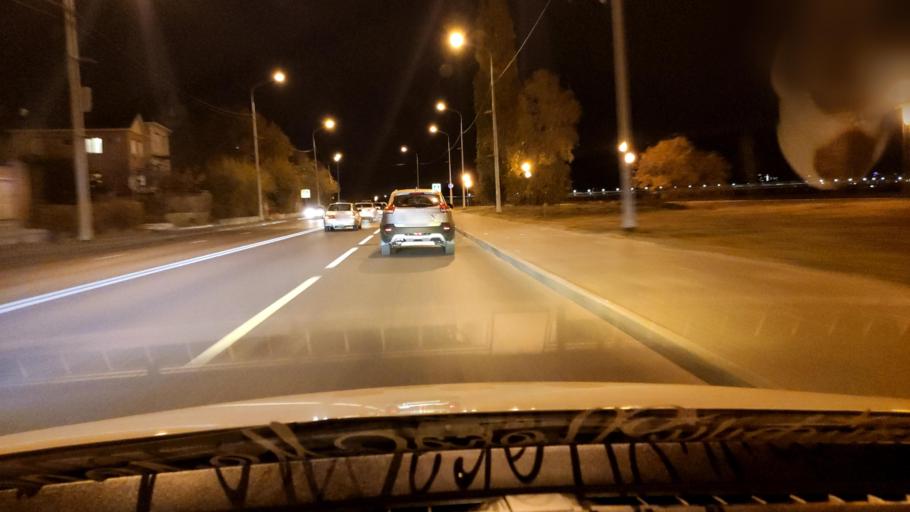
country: RU
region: Voronezj
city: Voronezh
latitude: 51.6795
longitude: 39.2276
